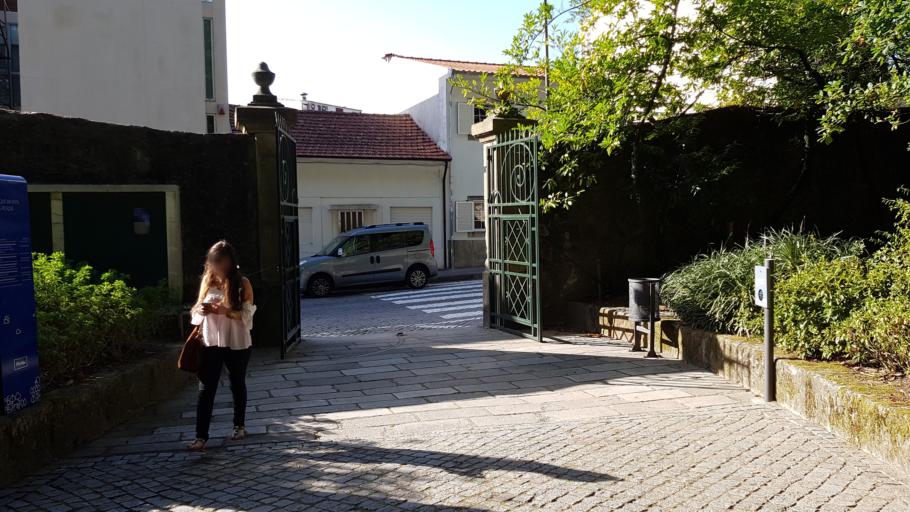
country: PT
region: Porto
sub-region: Porto
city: Porto
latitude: 41.1596
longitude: -8.5895
